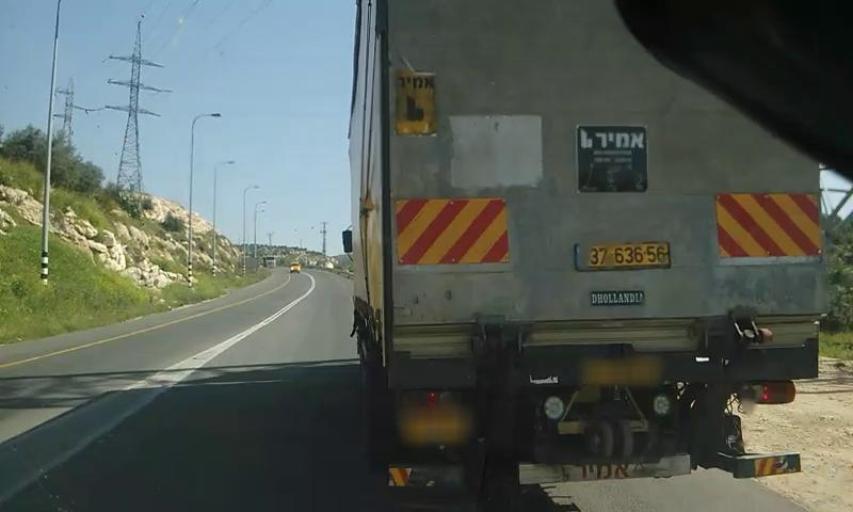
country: PS
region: West Bank
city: Idhna
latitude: 31.5693
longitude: 34.9872
